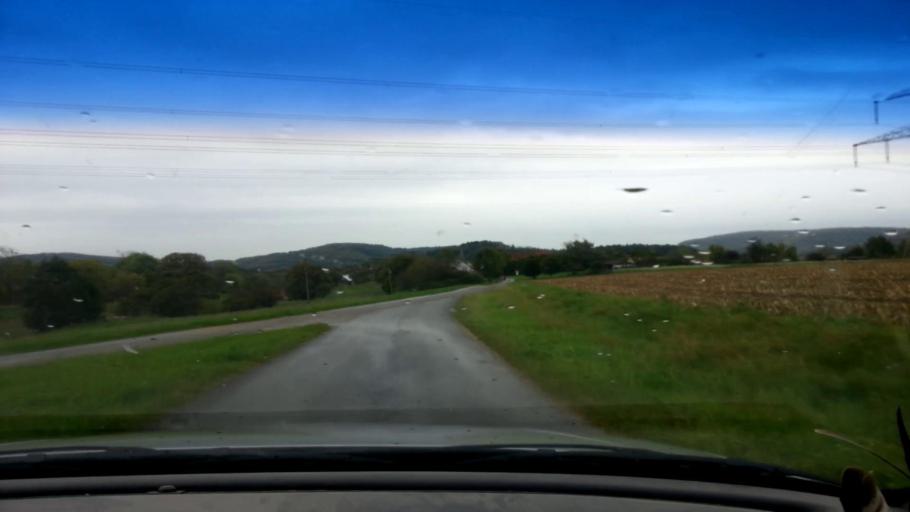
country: DE
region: Bavaria
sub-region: Upper Franconia
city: Poxdorf
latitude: 49.8914
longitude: 11.1038
